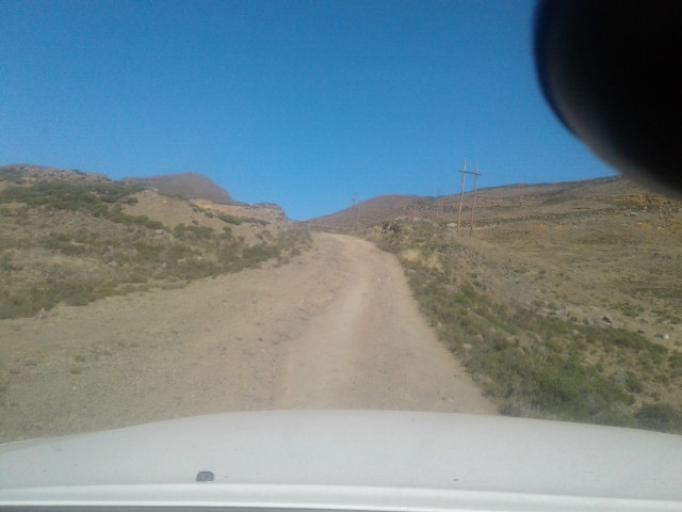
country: LS
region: Maseru
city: Nako
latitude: -29.3967
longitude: 28.0019
